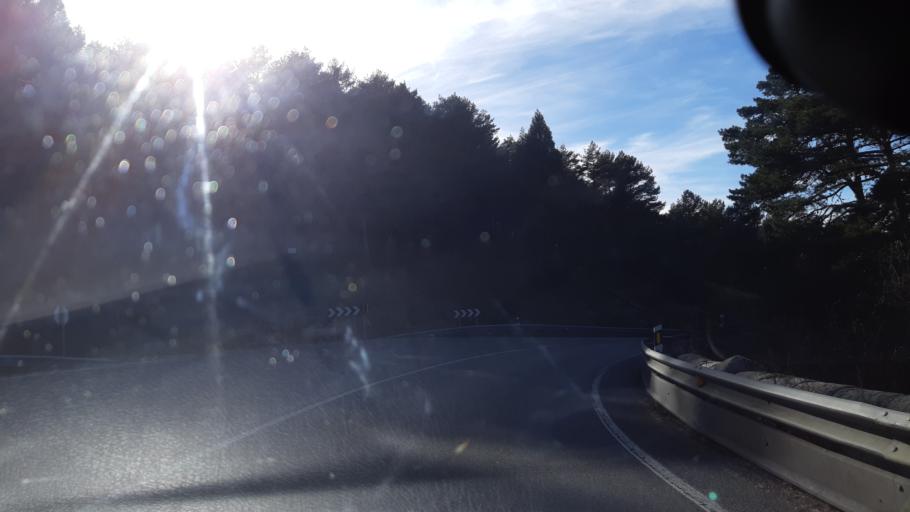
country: ES
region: Madrid
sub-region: Provincia de Madrid
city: Guadarrama
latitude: 40.7073
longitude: -4.1524
